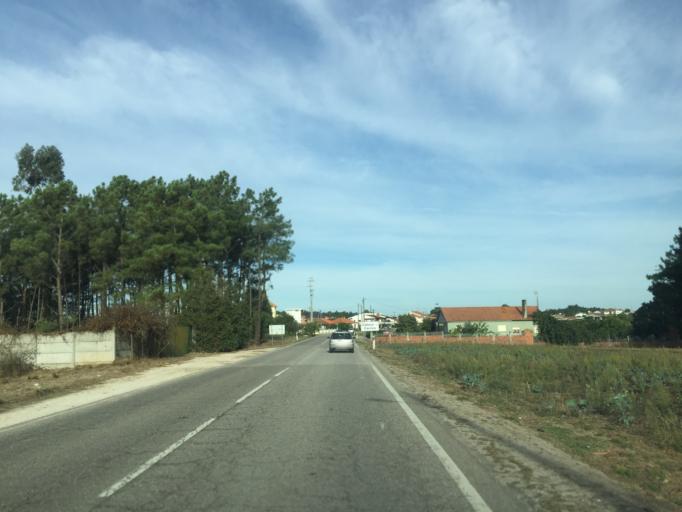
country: PT
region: Leiria
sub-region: Pombal
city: Lourical
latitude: 39.9728
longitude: -8.7949
